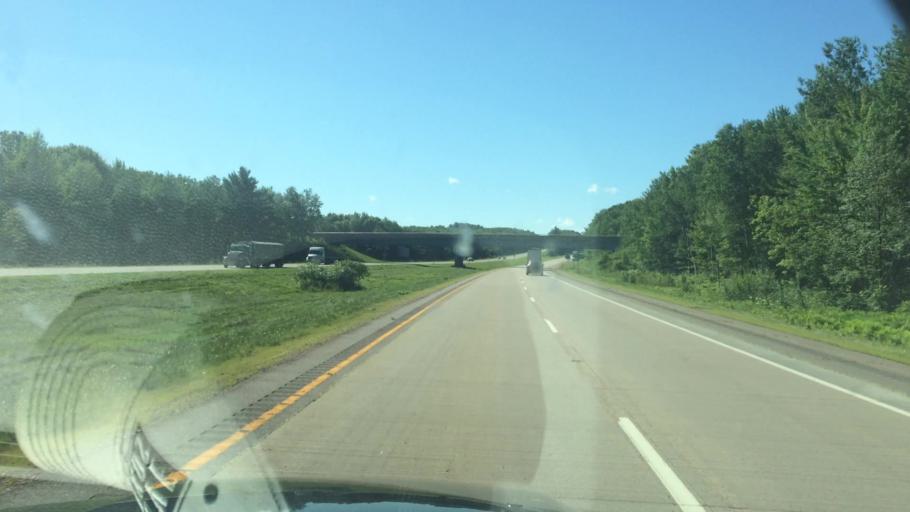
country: US
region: Wisconsin
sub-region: Marathon County
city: Mosinee
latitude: 44.7156
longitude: -89.6620
